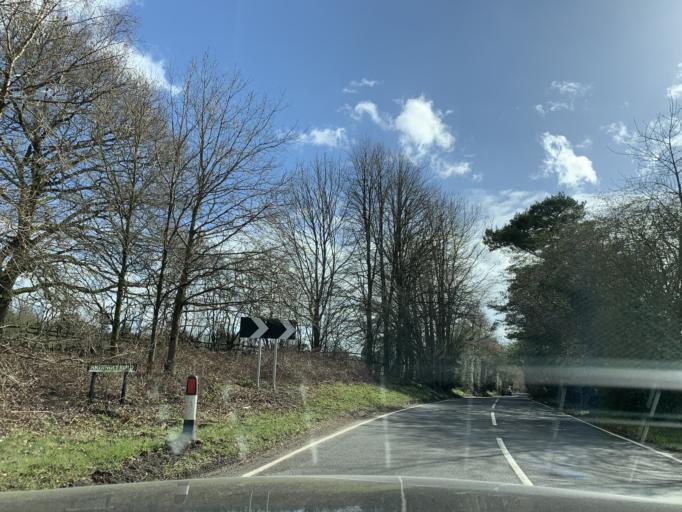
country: GB
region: England
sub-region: West Sussex
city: Crawley Down
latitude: 51.0912
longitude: -0.0759
